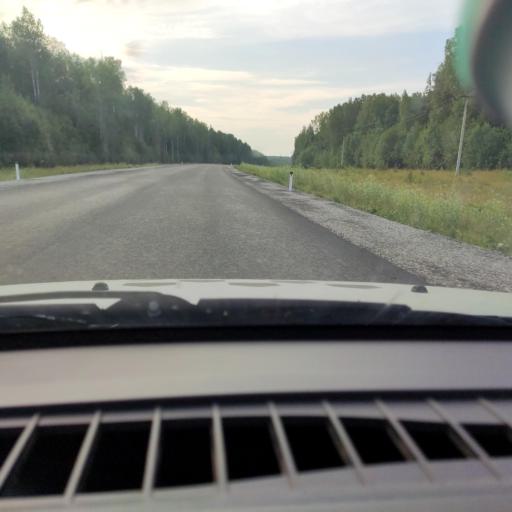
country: RU
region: Perm
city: Siva
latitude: 58.5969
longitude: 53.8774
